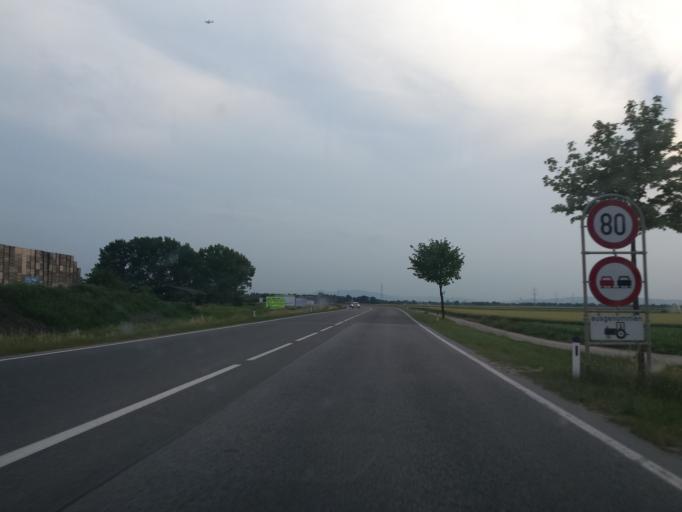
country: AT
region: Lower Austria
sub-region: Politischer Bezirk Ganserndorf
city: Aderklaa
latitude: 48.2880
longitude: 16.5404
